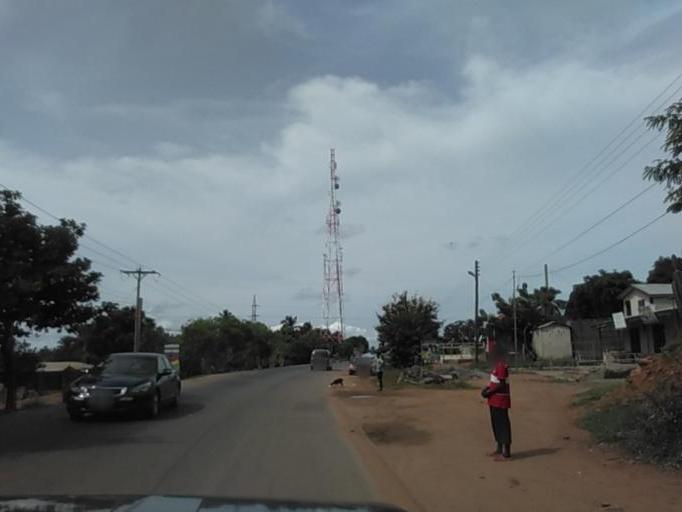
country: GH
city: Akropong
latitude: 6.2331
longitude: 0.0921
